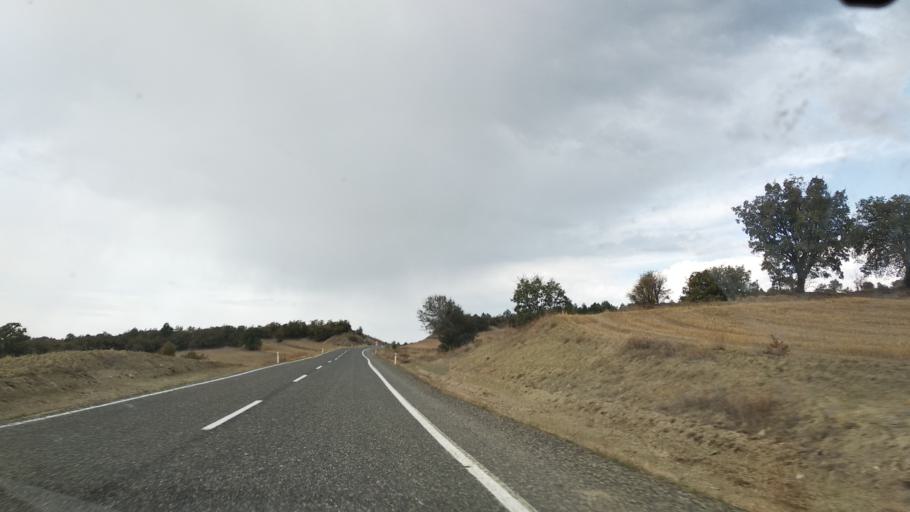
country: TR
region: Bolu
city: Seben
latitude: 40.3328
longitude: 31.4476
